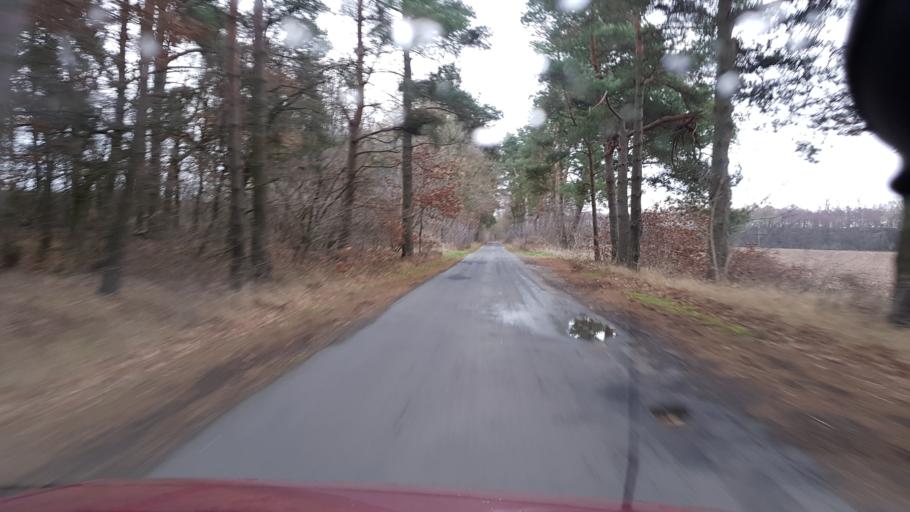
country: PL
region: West Pomeranian Voivodeship
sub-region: Powiat stargardzki
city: Stargard Szczecinski
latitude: 53.3275
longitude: 15.1172
